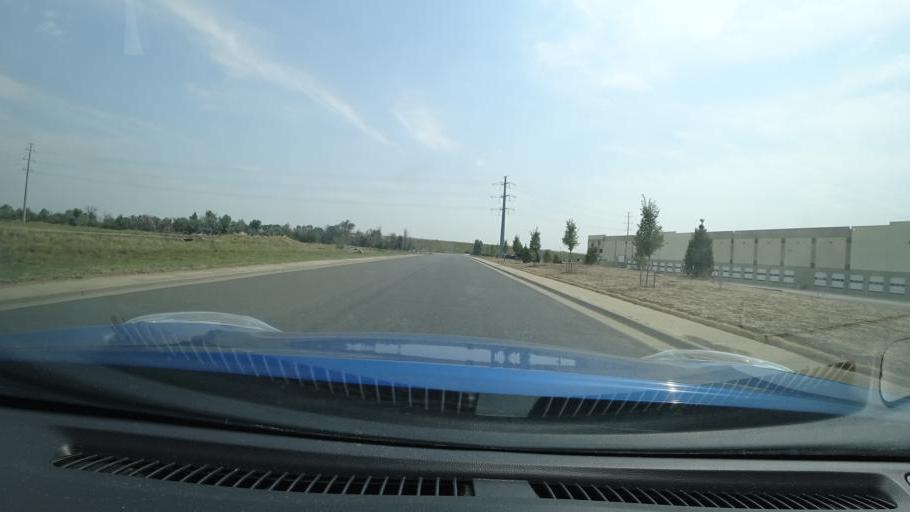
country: US
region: Colorado
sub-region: Adams County
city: Aurora
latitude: 39.7562
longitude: -104.7534
